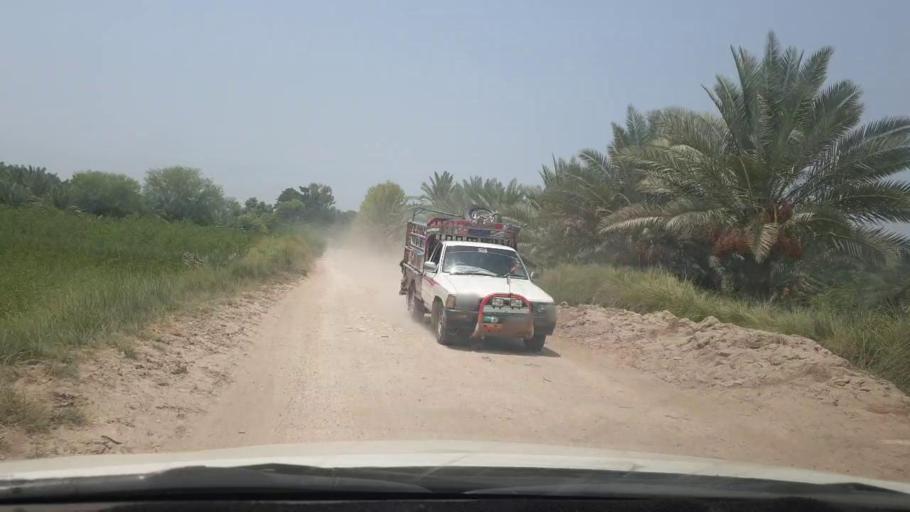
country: PK
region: Sindh
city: Khairpur
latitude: 27.5032
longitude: 68.8661
